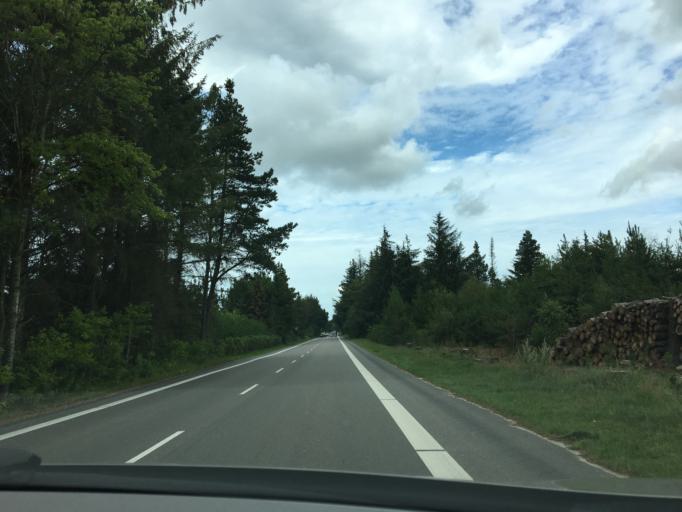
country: DK
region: South Denmark
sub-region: Varde Kommune
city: Oksbol
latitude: 55.7752
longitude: 8.2379
